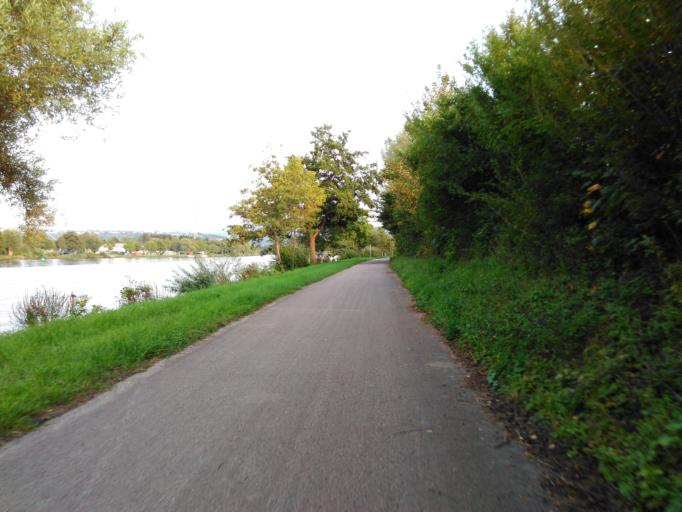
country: DE
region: Rheinland-Pfalz
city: Wasserliesch
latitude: 49.7060
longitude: 6.5481
